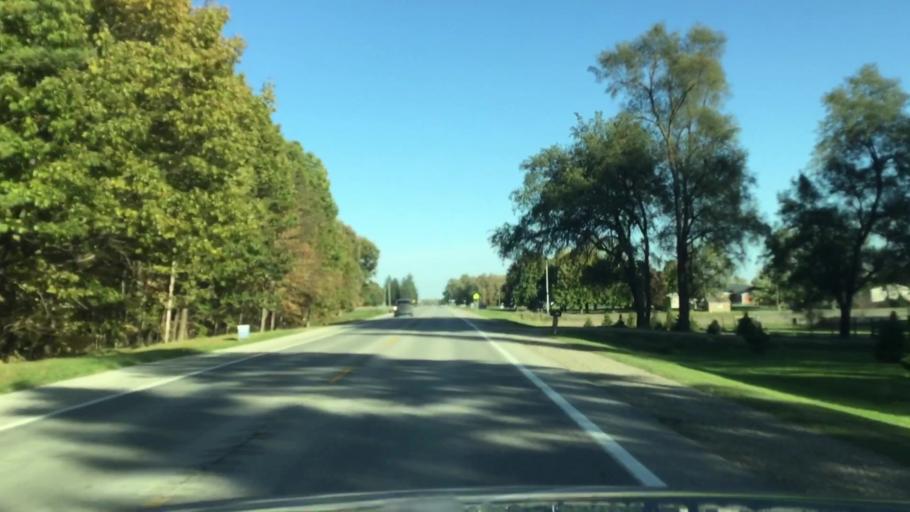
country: US
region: Michigan
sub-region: Lapeer County
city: North Branch
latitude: 43.2283
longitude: -83.2339
